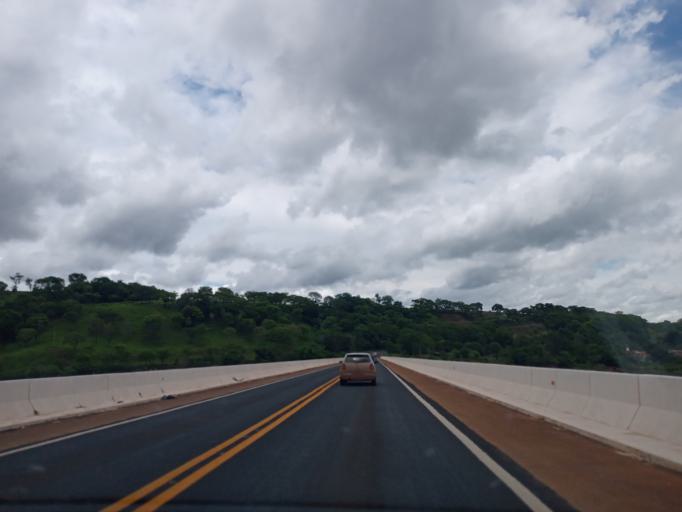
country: BR
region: Minas Gerais
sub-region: Monte Carmelo
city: Monte Carmelo
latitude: -19.2677
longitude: -47.6401
